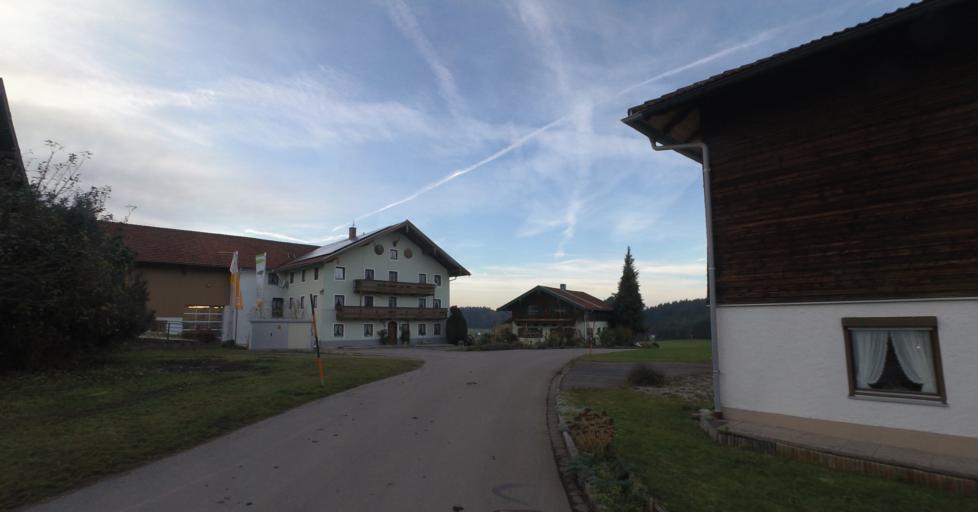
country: DE
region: Bavaria
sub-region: Upper Bavaria
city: Nussdorf
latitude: 47.8934
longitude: 12.5968
